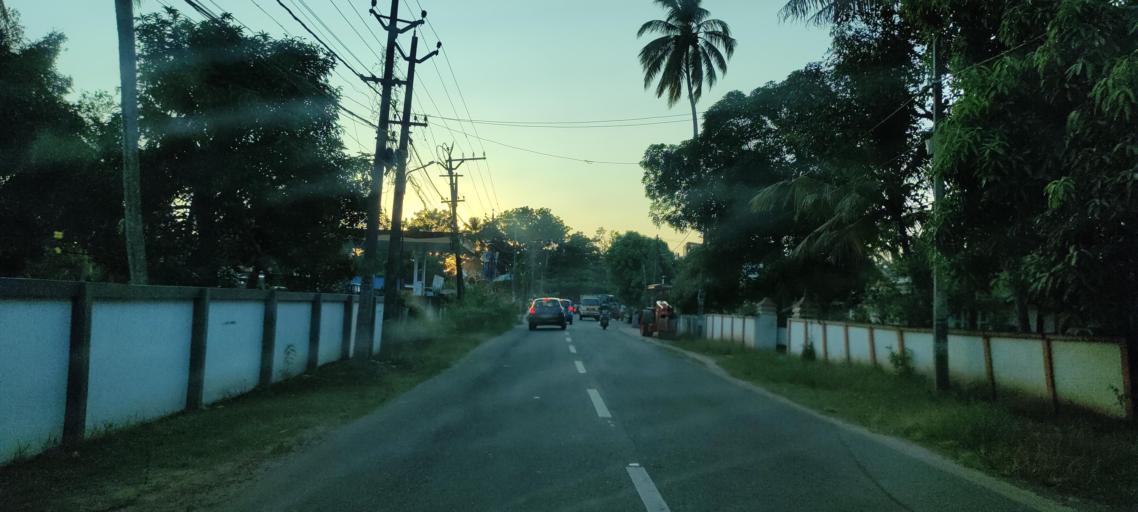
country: IN
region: Kerala
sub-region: Alappuzha
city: Kayankulam
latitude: 9.2583
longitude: 76.4278
